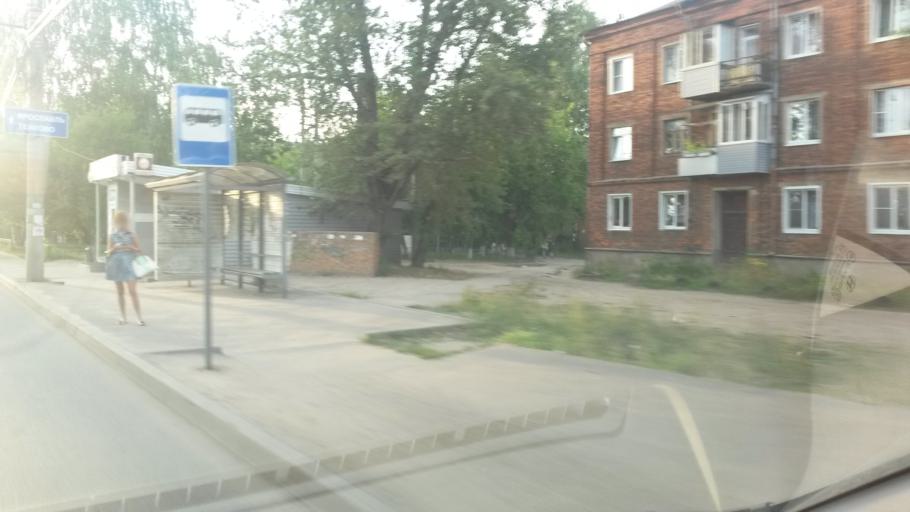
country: RU
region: Ivanovo
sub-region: Gorod Ivanovo
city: Ivanovo
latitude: 57.0097
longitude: 40.9428
